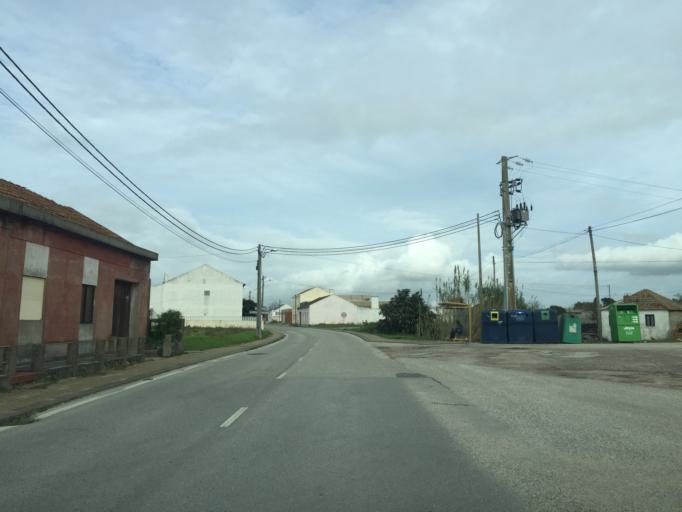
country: PT
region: Coimbra
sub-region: Figueira da Foz
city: Lavos
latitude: 40.0551
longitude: -8.8146
